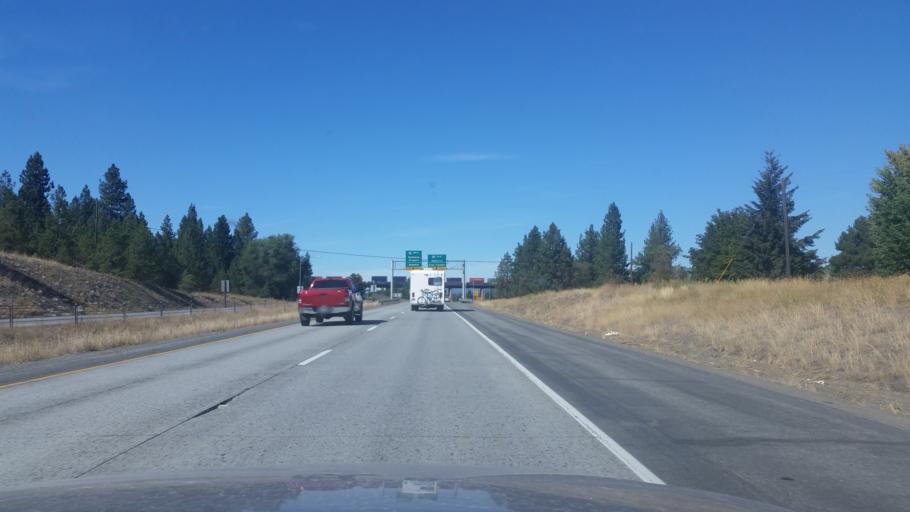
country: US
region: Washington
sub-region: Spokane County
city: Spokane
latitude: 47.6423
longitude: -117.4489
